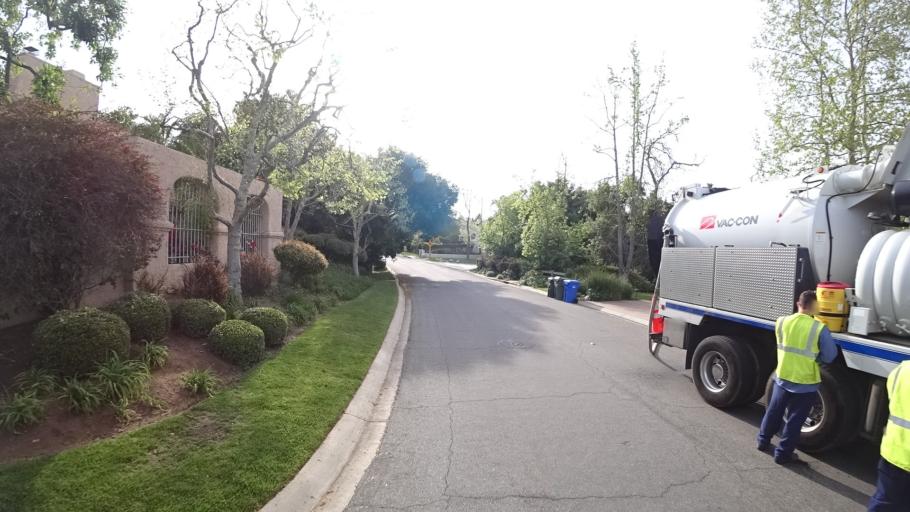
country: US
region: California
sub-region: Ventura County
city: Thousand Oaks
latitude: 34.1944
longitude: -118.8121
